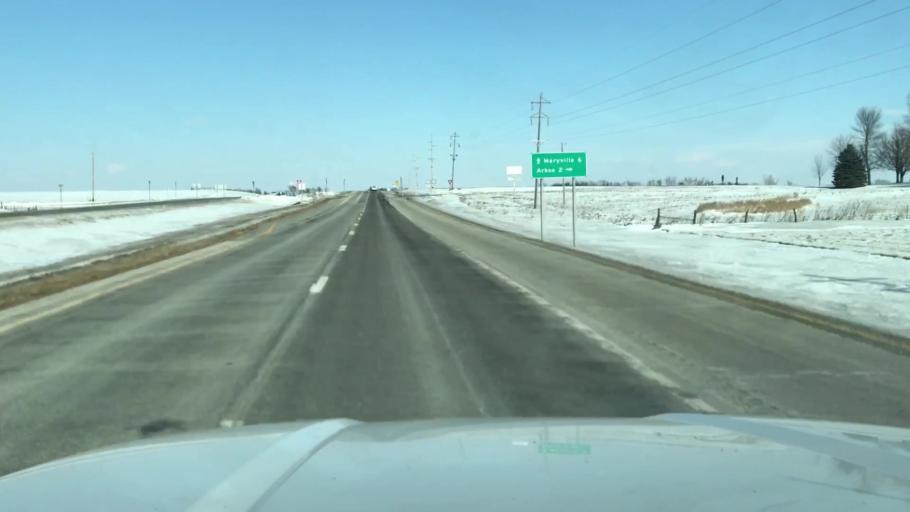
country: US
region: Missouri
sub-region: Nodaway County
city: Maryville
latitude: 40.2569
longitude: -94.8668
